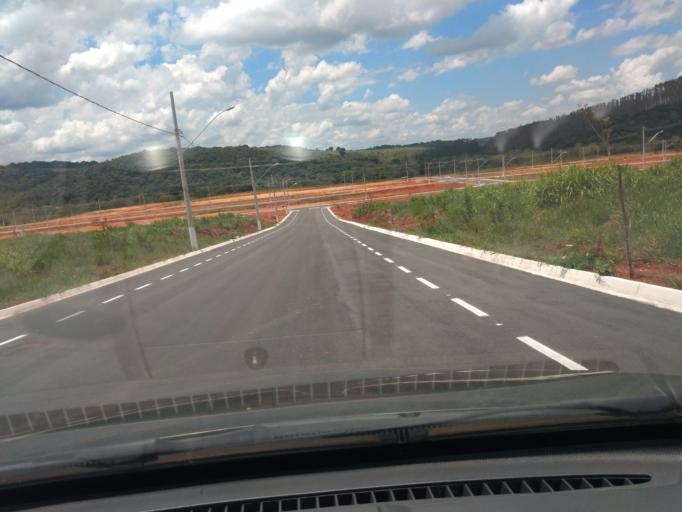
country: BR
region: Minas Gerais
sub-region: Tres Coracoes
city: Tres Coracoes
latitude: -21.6638
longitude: -45.2755
